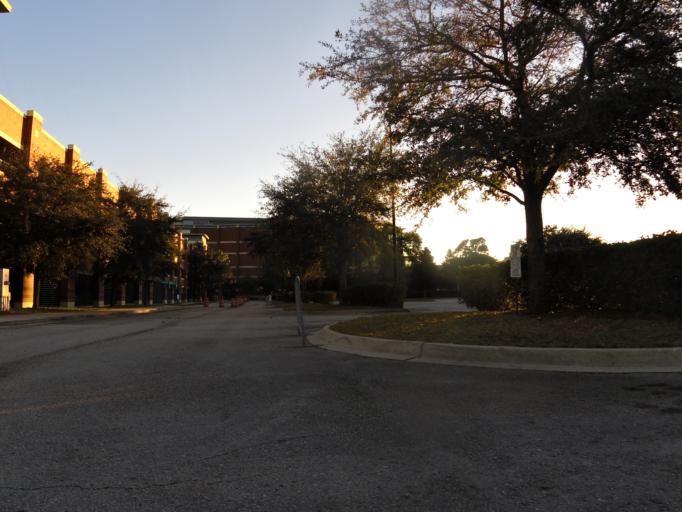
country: US
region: Florida
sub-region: Duval County
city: Jacksonville
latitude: 30.3277
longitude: -81.6442
